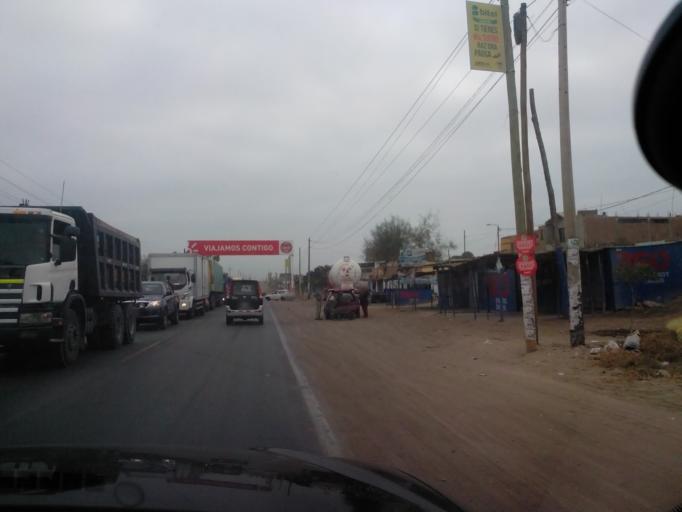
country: PE
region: Ica
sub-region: Provincia de Pisco
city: Villa Tupac Amaru
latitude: -13.7116
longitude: -76.1529
